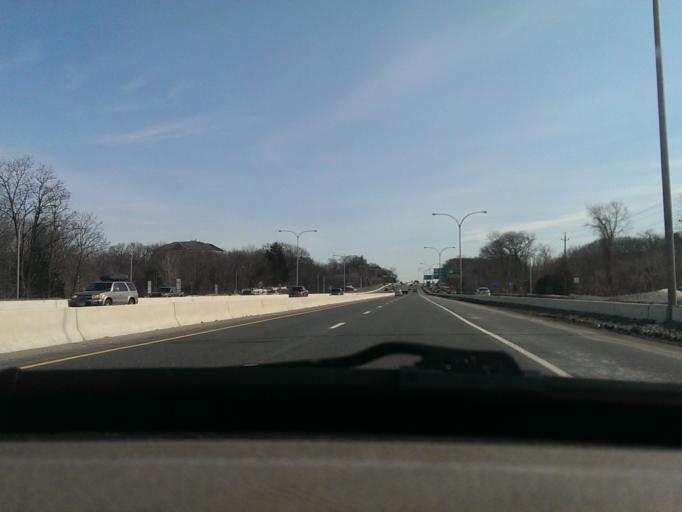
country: US
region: Rhode Island
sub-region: Providence County
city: Cumberland Hill
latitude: 41.9420
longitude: -71.4748
